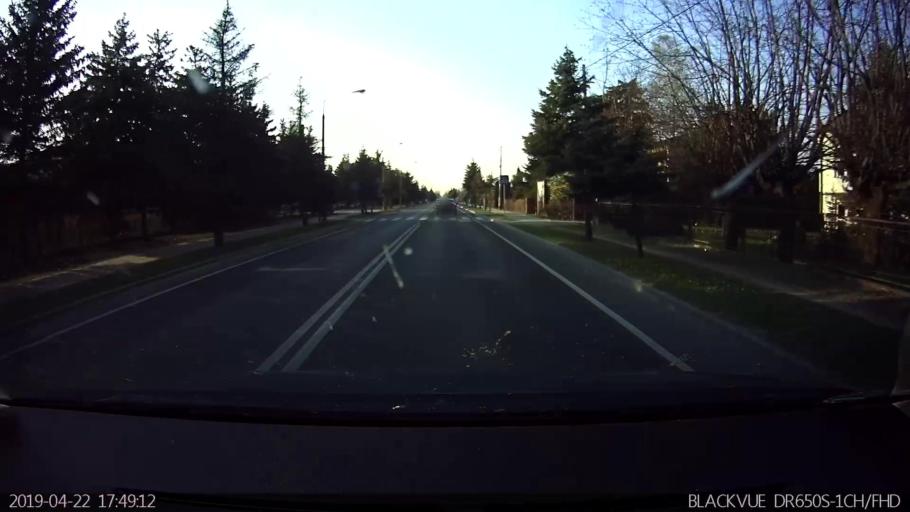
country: PL
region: Masovian Voivodeship
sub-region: Powiat wegrowski
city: Wegrow
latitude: 52.4119
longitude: 22.0102
